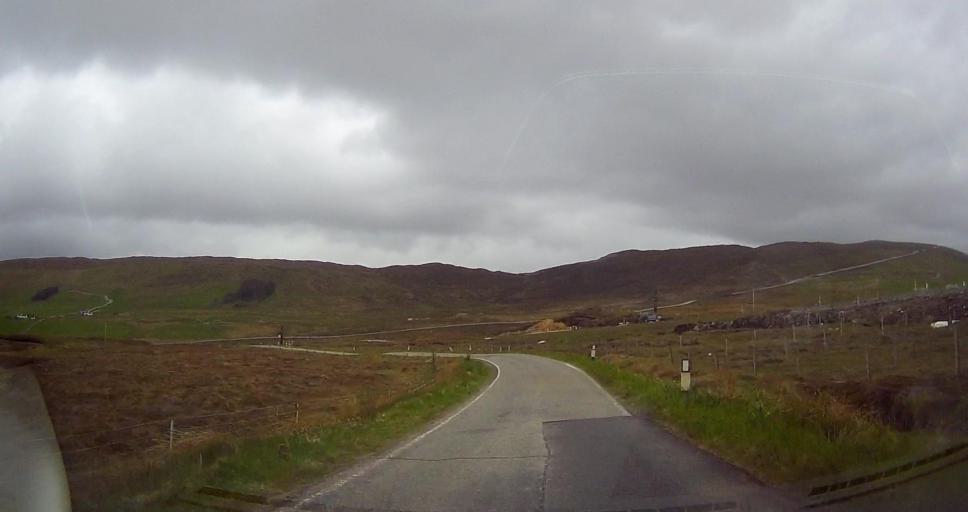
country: GB
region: Scotland
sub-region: Shetland Islands
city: Lerwick
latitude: 60.2779
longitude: -1.2665
